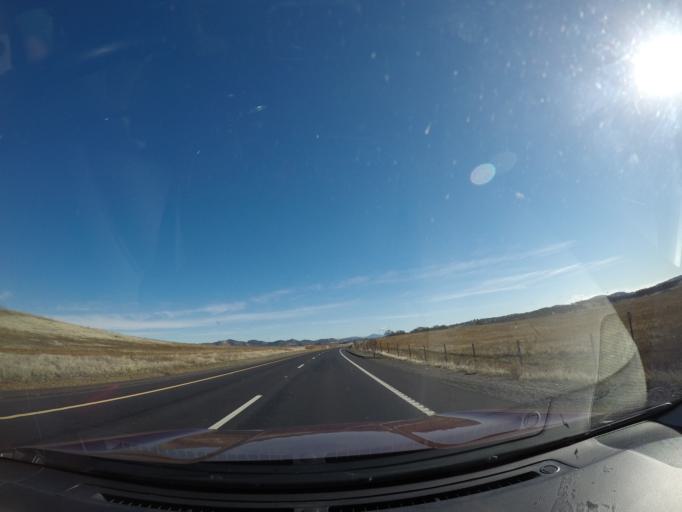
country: US
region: California
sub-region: Calaveras County
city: Copperopolis
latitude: 37.8462
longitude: -120.5554
